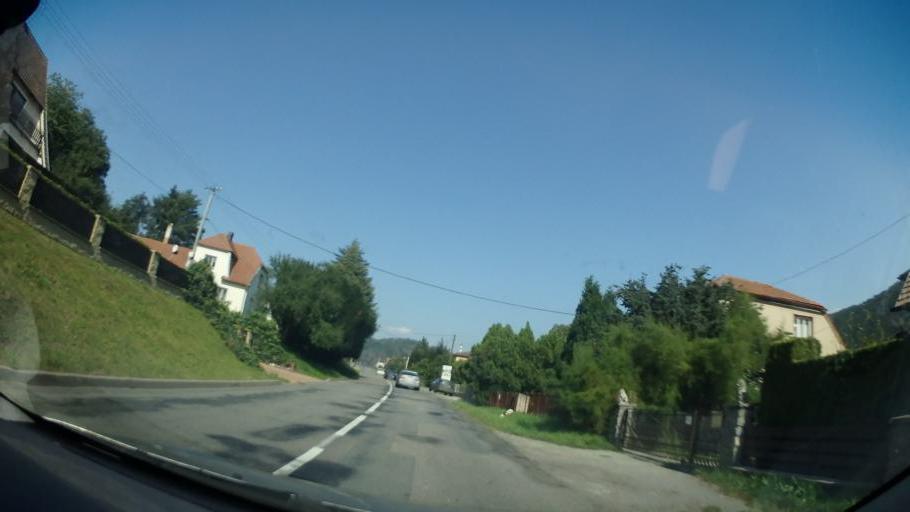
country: CZ
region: South Moravian
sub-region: Okres Brno-Venkov
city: Nedvedice
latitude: 49.4506
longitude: 16.3415
